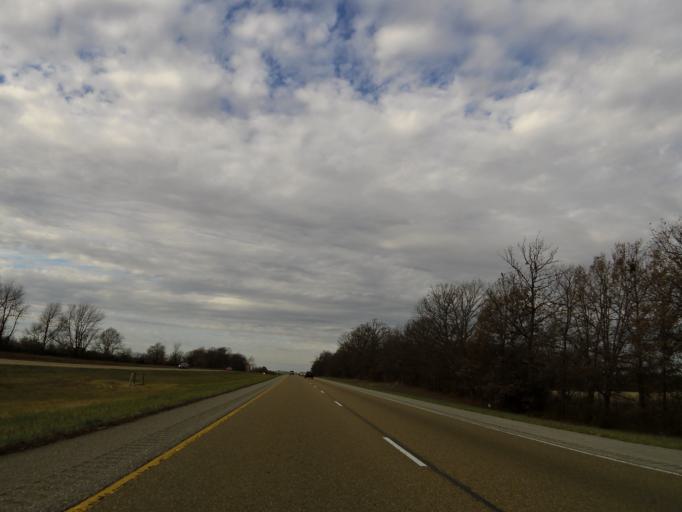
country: US
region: Illinois
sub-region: Clinton County
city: Wamac
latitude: 38.3893
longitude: -89.2076
